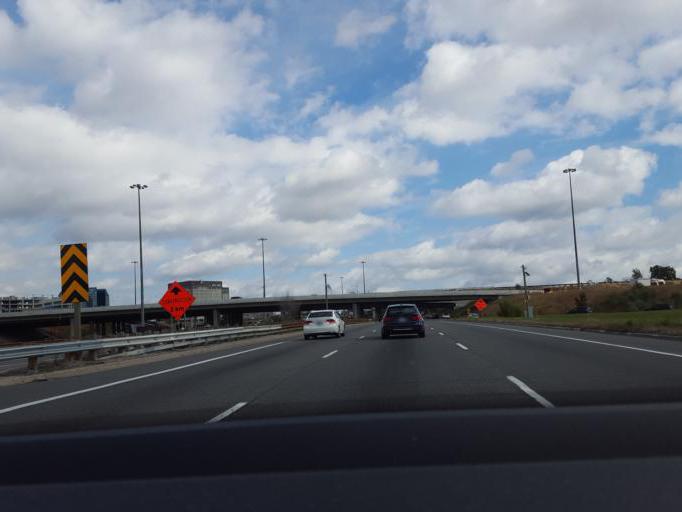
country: CA
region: Ontario
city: Willowdale
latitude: 43.7668
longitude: -79.3416
